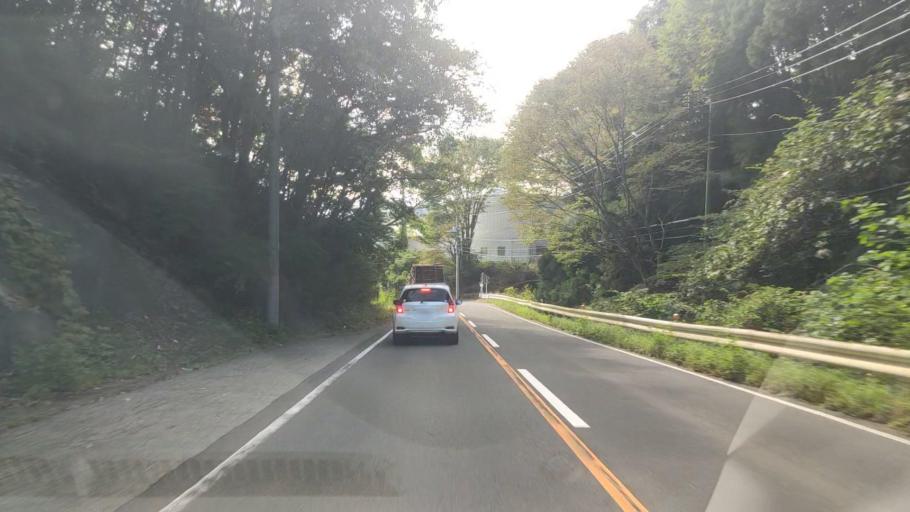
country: JP
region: Gunma
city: Numata
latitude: 36.6286
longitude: 139.0122
